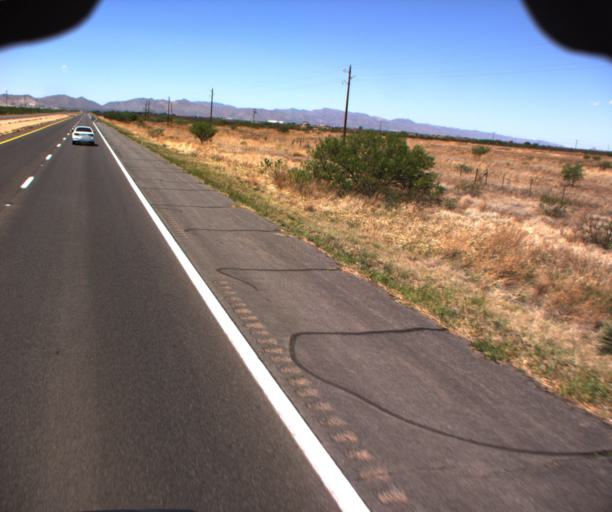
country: US
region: Arizona
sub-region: Cochise County
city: Pirtleville
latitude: 31.3604
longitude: -109.6605
